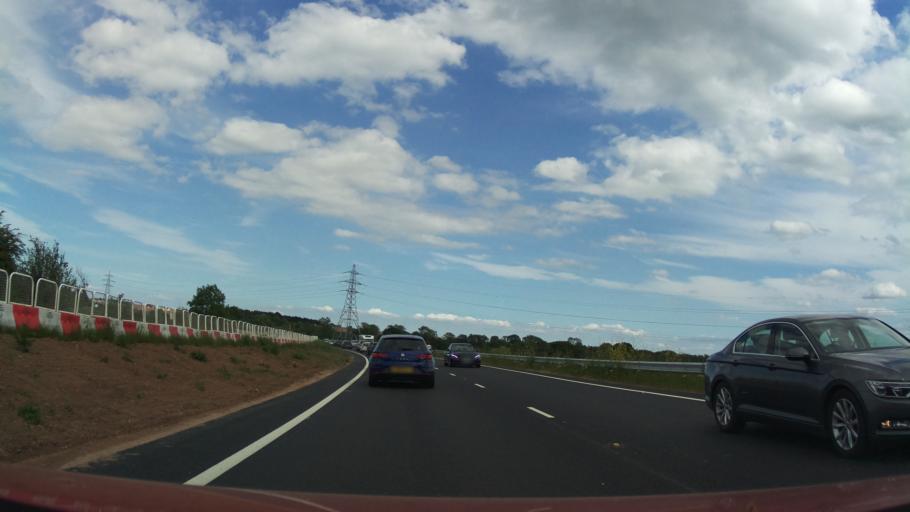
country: GB
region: England
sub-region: Worcestershire
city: Kempsey
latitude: 52.1624
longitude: -2.2272
